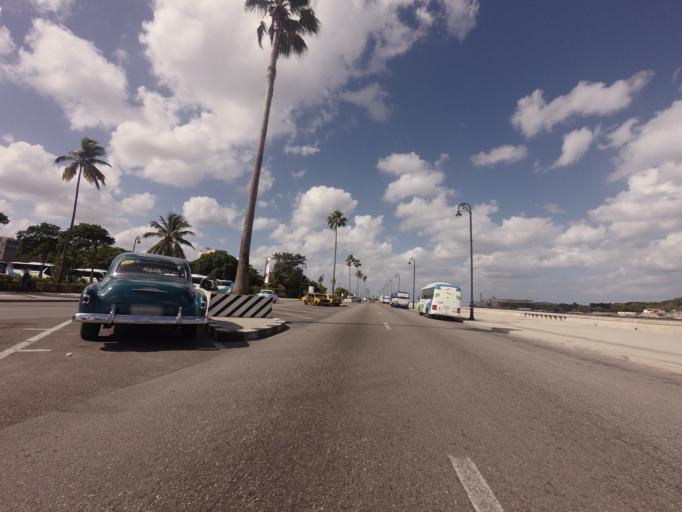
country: CU
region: La Habana
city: La Habana Vieja
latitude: 23.1430
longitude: -82.3513
